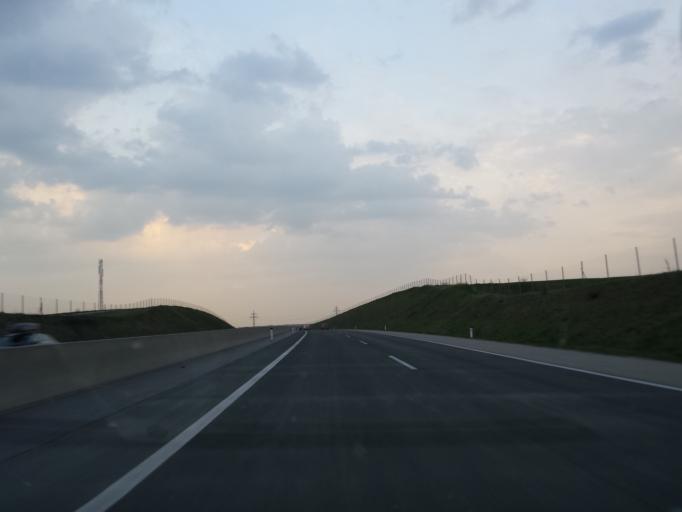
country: AT
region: Lower Austria
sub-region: Politischer Bezirk Mistelbach
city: Hochleithen
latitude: 48.4572
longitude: 16.5523
